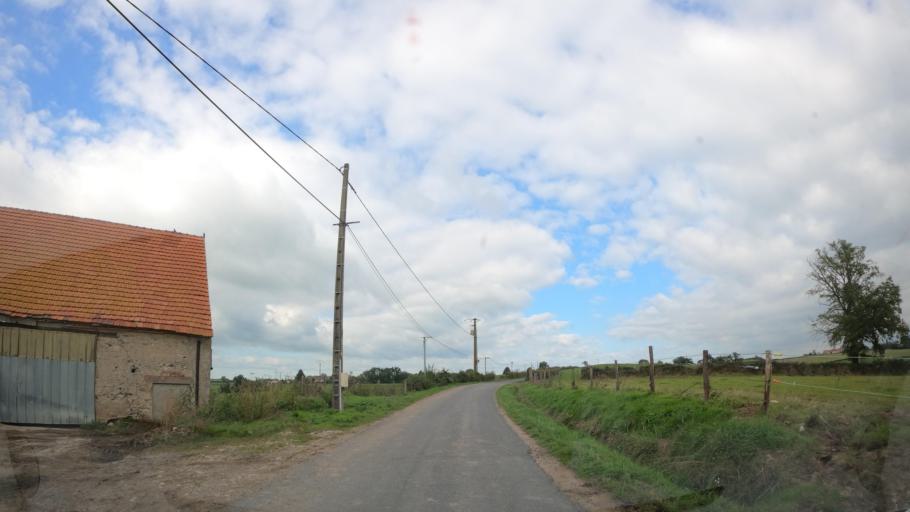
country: FR
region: Auvergne
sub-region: Departement de l'Allier
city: Lapalisse
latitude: 46.3387
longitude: 3.6373
